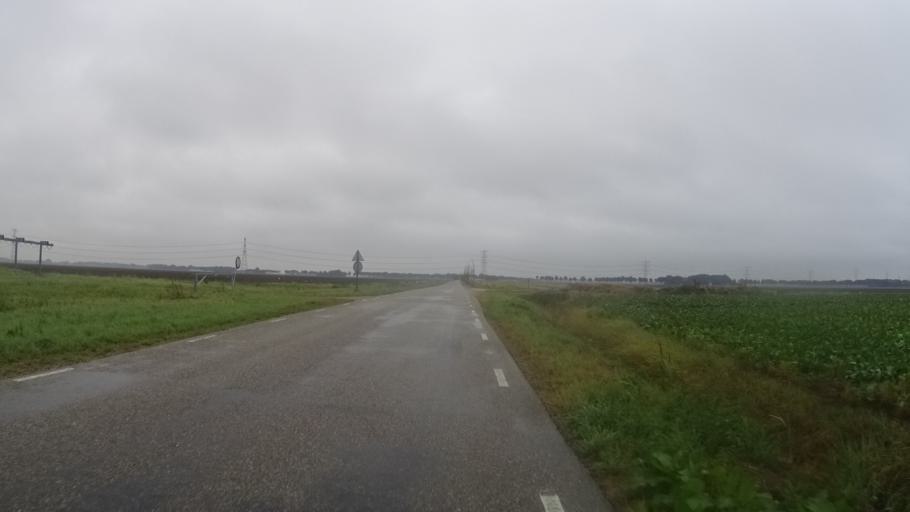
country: NL
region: Groningen
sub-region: Gemeente Veendam
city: Veendam
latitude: 53.1919
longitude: 6.9015
